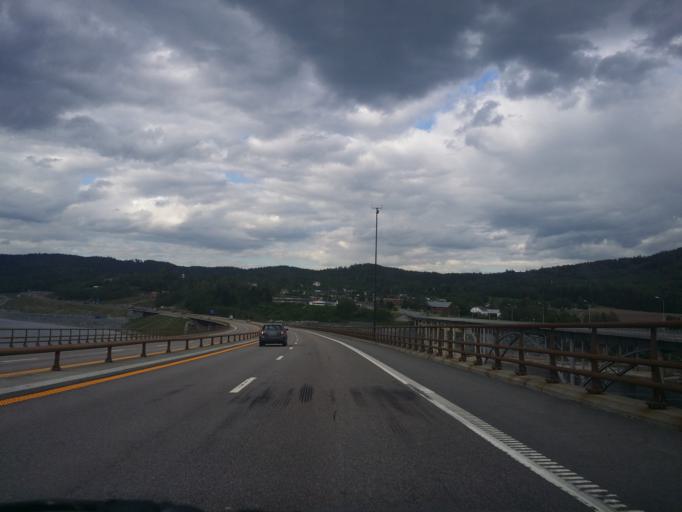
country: NO
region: Akershus
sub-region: Eidsvoll
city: Eidsvoll
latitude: 60.3976
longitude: 11.2298
